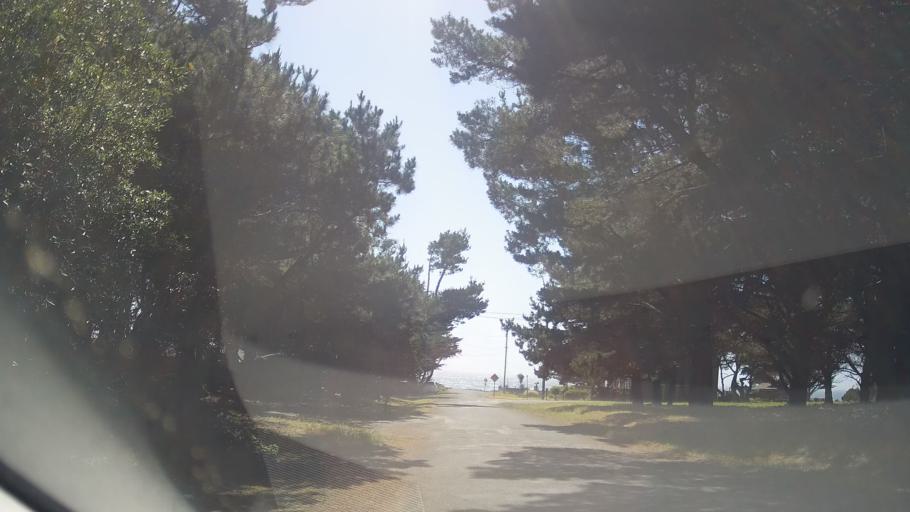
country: US
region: California
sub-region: Mendocino County
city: Fort Bragg
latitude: 39.4193
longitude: -123.8129
